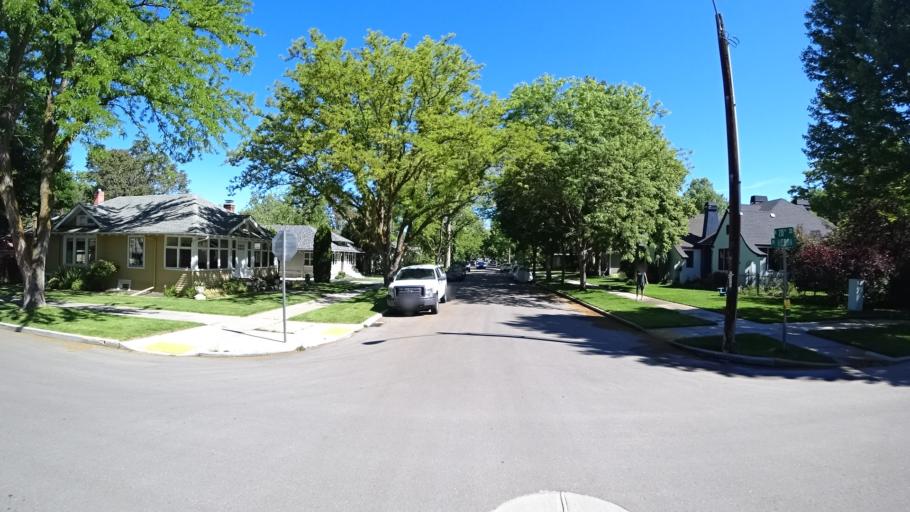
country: US
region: Idaho
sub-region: Ada County
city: Boise
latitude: 43.6338
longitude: -116.2134
